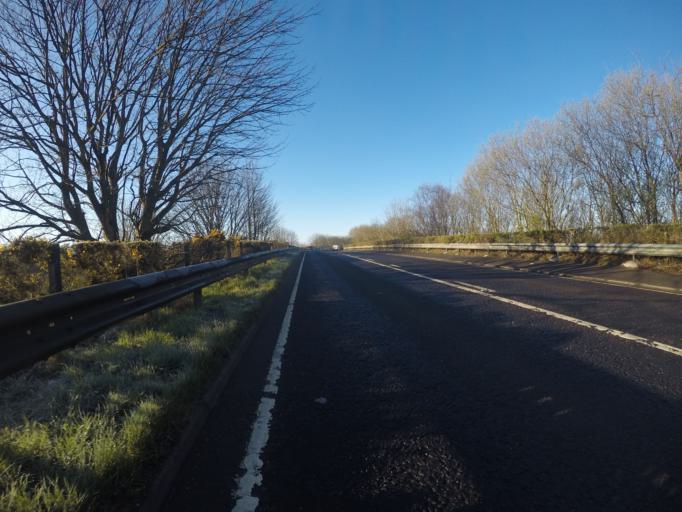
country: GB
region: Scotland
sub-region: North Ayrshire
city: Stevenston
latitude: 55.6373
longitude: -4.7403
